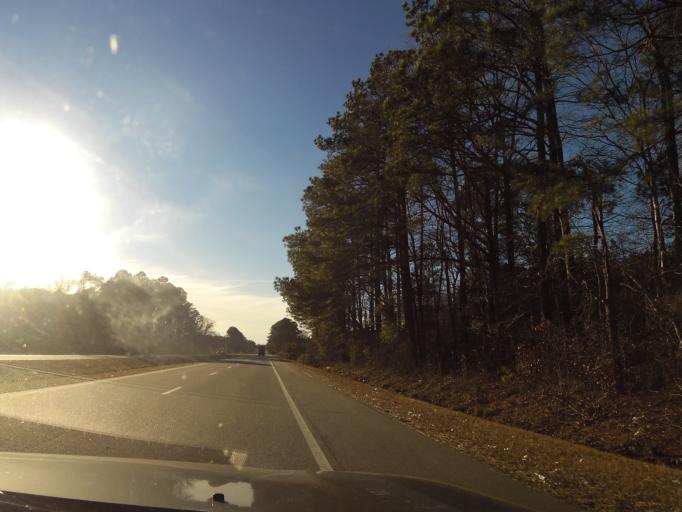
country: US
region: Virginia
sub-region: City of Franklin
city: Franklin
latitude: 36.6532
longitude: -76.8320
